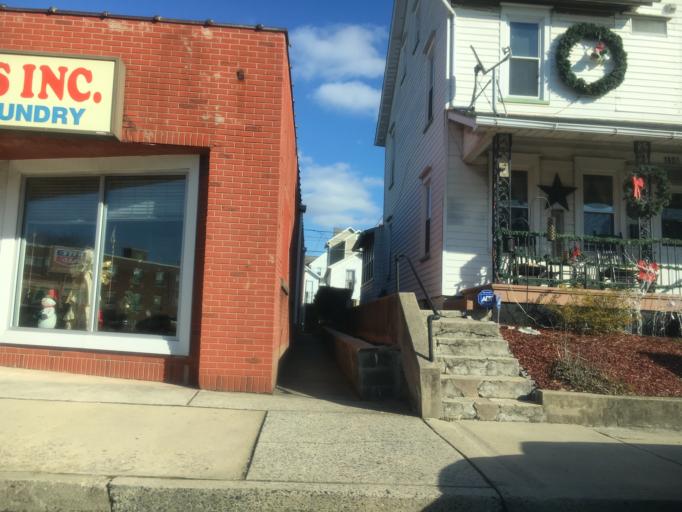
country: US
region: Pennsylvania
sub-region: Northampton County
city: Northampton
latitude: 40.6852
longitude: -75.4958
